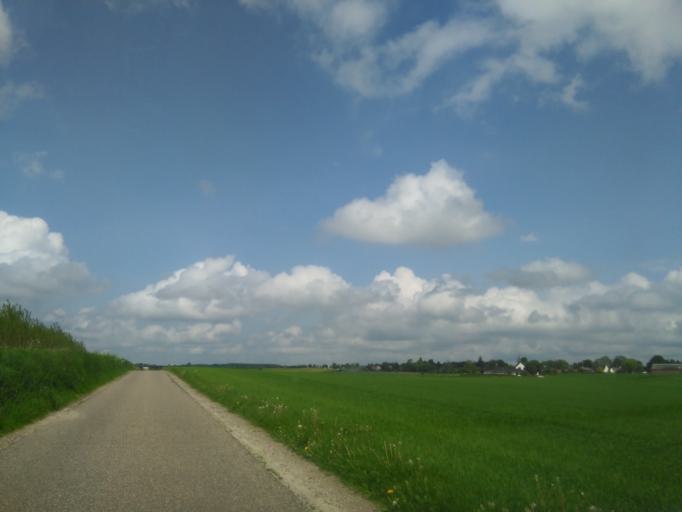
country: DK
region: Central Jutland
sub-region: Arhus Kommune
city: Sabro
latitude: 56.2153
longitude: 9.9796
